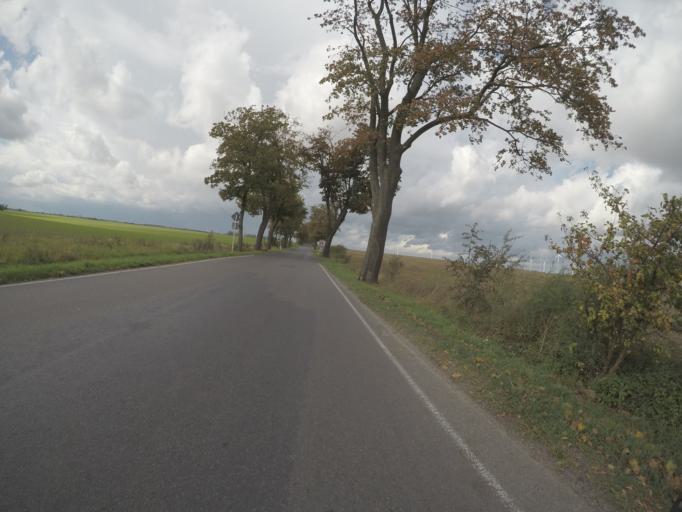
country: DE
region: Brandenburg
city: Altlandsberg
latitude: 52.5858
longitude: 13.7858
